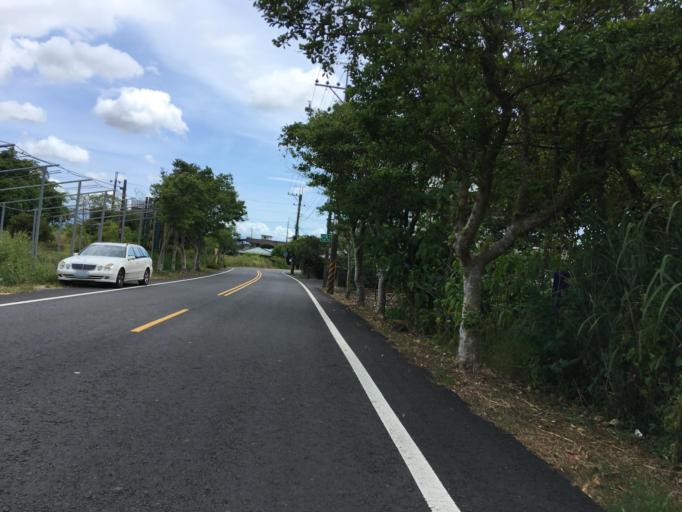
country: TW
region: Taiwan
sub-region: Yilan
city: Yilan
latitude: 24.6310
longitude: 121.7118
